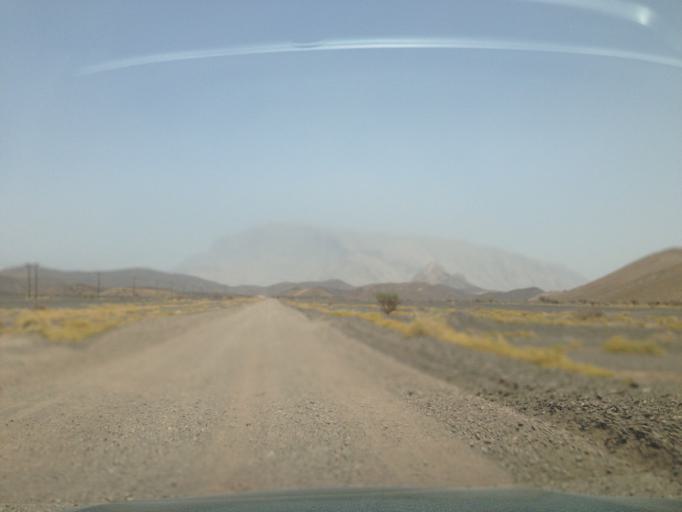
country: OM
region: Az Zahirah
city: `Ibri
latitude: 23.2060
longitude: 56.8512
